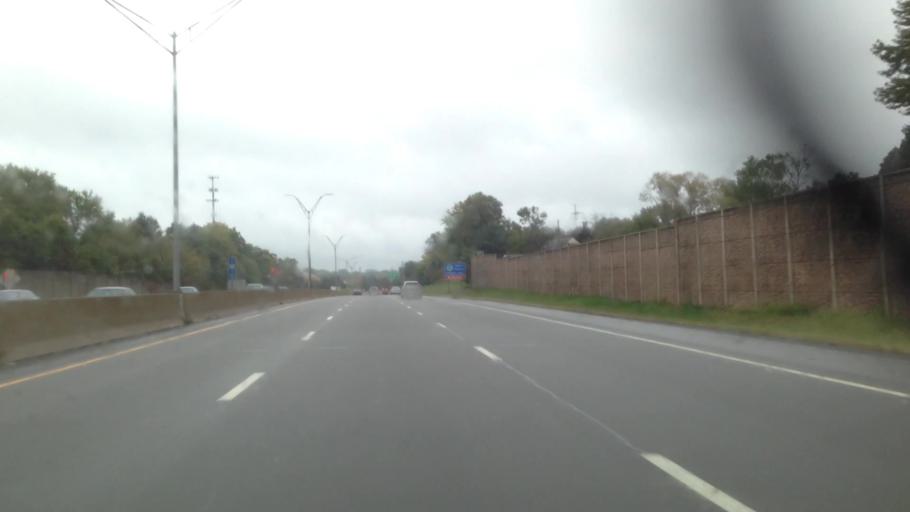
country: US
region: Ohio
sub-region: Summit County
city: Silver Lake
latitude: 41.1543
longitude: -81.4704
